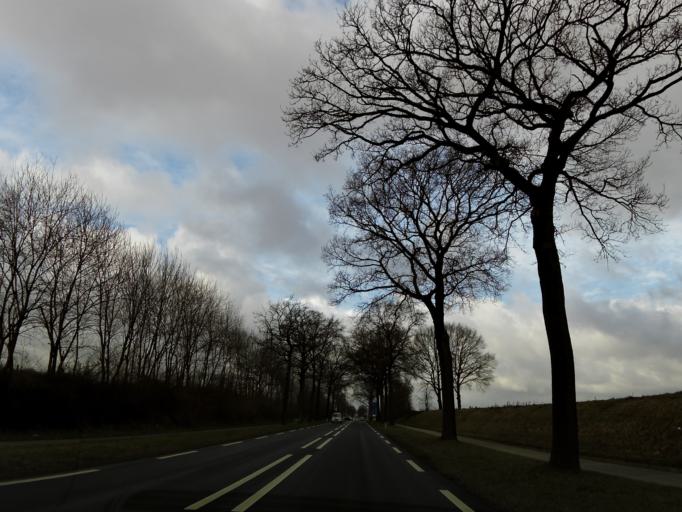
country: NL
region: Limburg
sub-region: Eijsden-Margraten
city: Margraten
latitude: 50.8146
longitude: 5.8505
